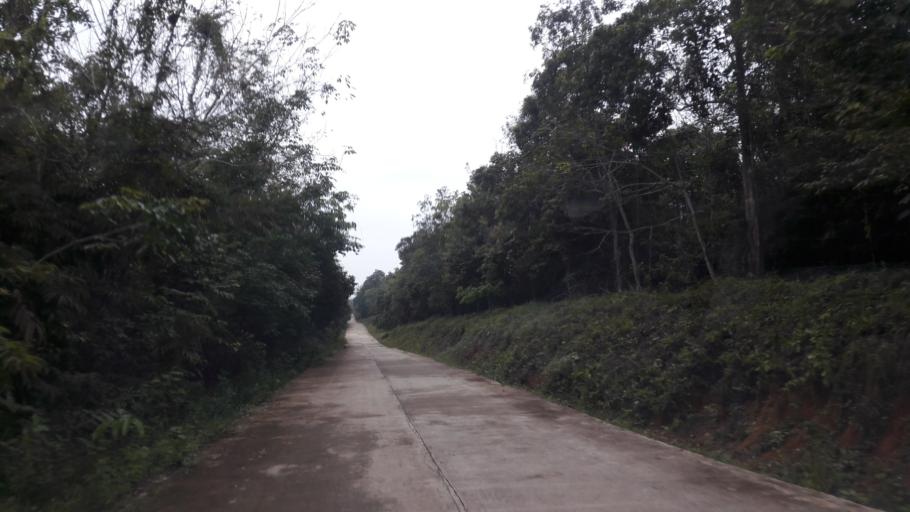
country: ID
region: South Sumatra
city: Gunungmenang
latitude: -3.1984
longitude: 103.8650
